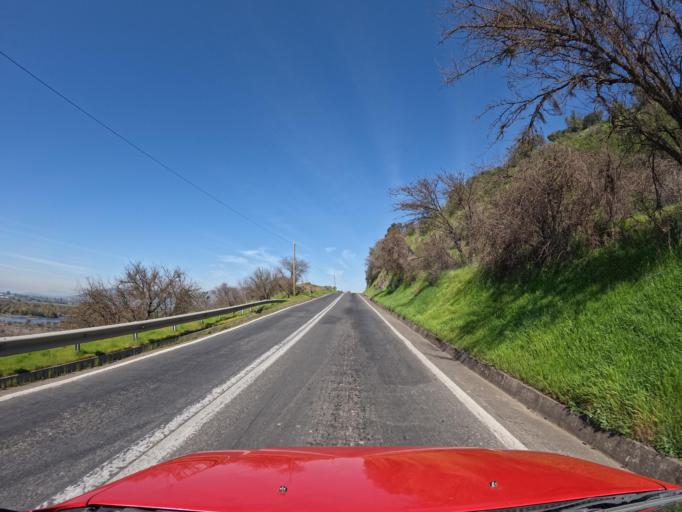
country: CL
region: Maule
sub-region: Provincia de Curico
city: Rauco
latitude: -34.9745
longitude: -71.3825
